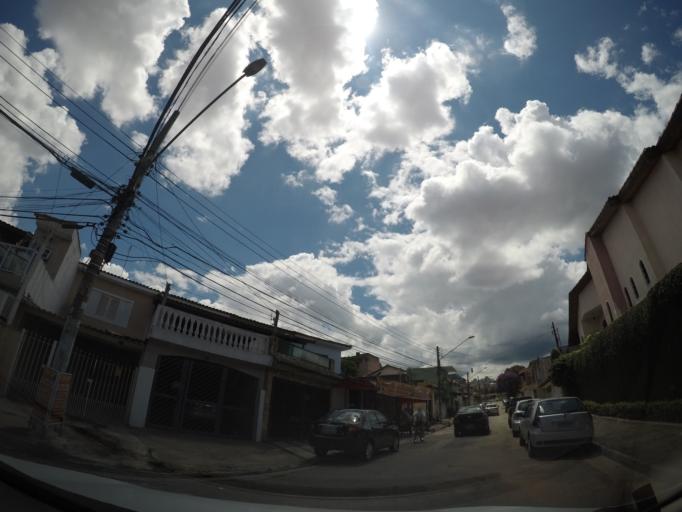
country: BR
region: Sao Paulo
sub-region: Guarulhos
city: Guarulhos
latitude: -23.4504
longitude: -46.5366
